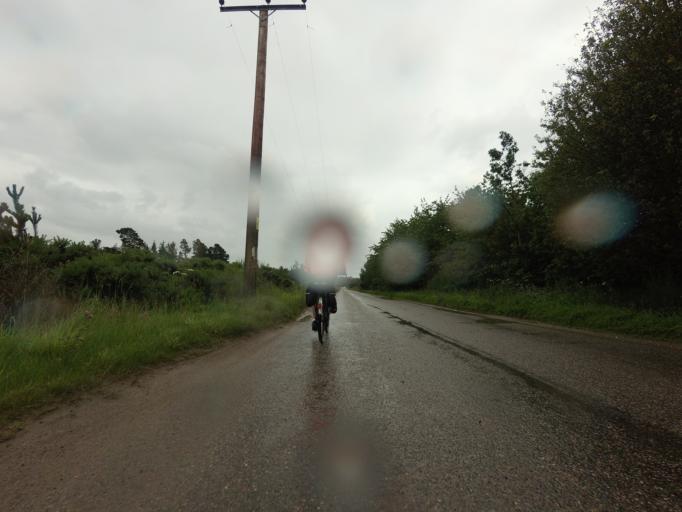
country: GB
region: Scotland
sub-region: Moray
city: Fochabers
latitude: 57.6609
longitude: -3.0593
